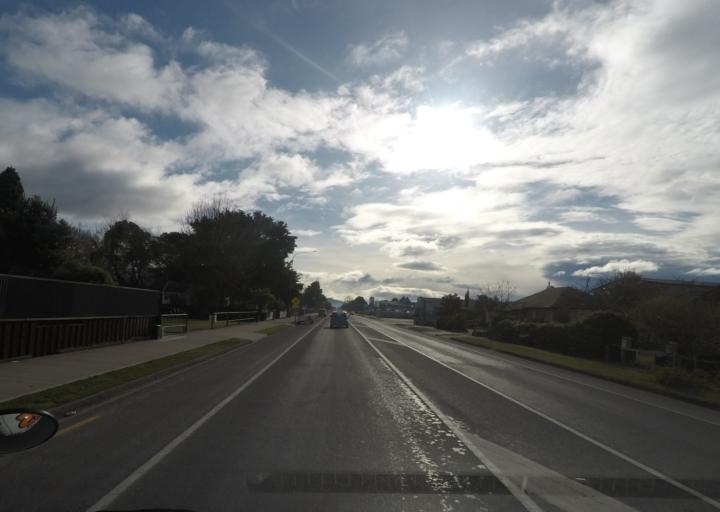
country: NZ
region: Tasman
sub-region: Tasman District
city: Motueka
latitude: -41.1317
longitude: 173.0100
